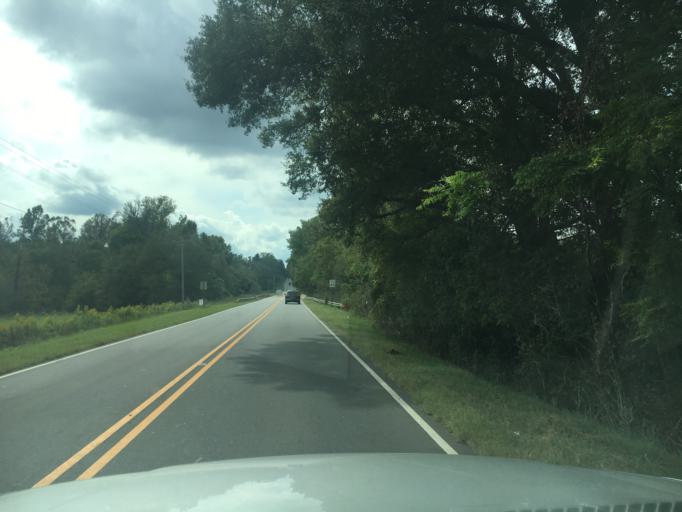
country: US
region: North Carolina
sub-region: Gaston County
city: Dallas
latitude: 35.3033
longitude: -81.2203
